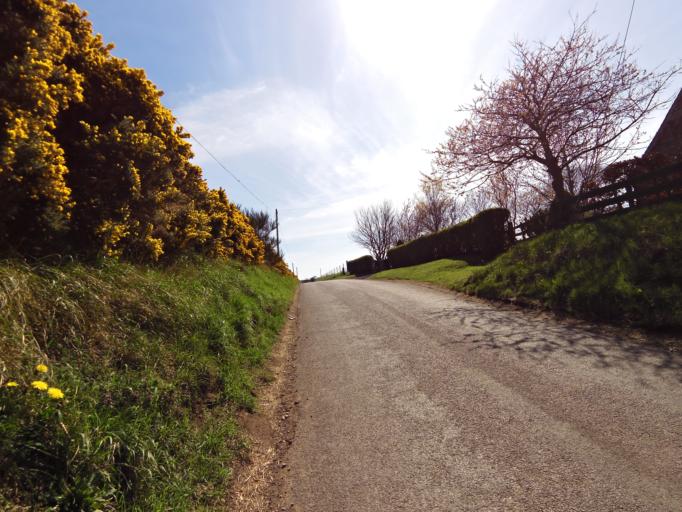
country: GB
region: Scotland
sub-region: Angus
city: Montrose
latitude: 56.6484
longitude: -2.5140
